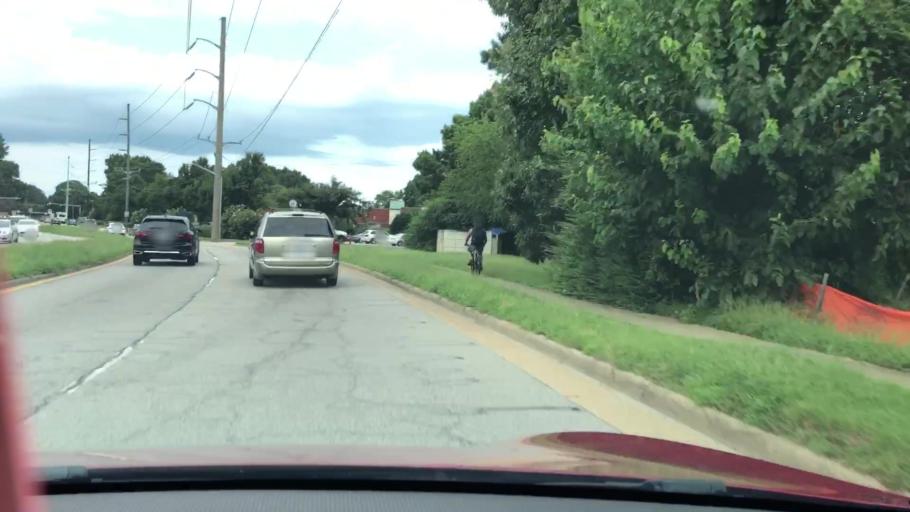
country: US
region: Virginia
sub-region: City of Virginia Beach
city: Virginia Beach
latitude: 36.8533
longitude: -76.0227
